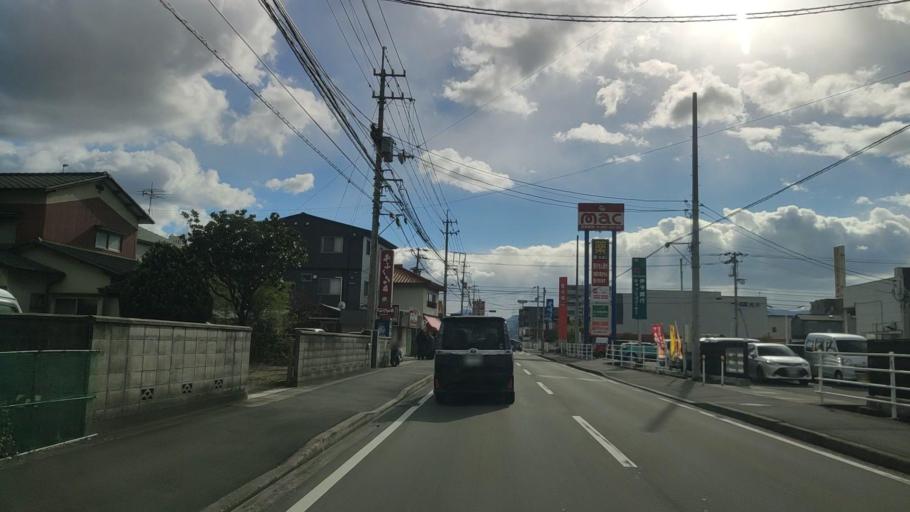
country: JP
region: Ehime
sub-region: Shikoku-chuo Shi
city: Matsuyama
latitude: 33.8106
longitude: 132.7953
